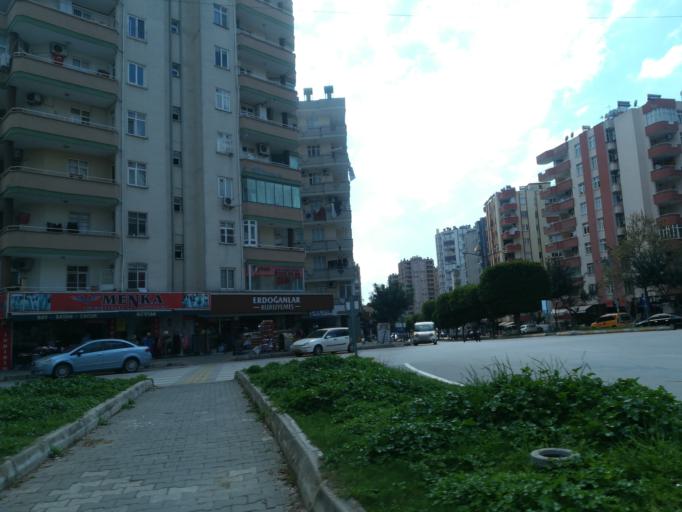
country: TR
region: Adana
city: Adana
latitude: 37.0313
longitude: 35.3009
